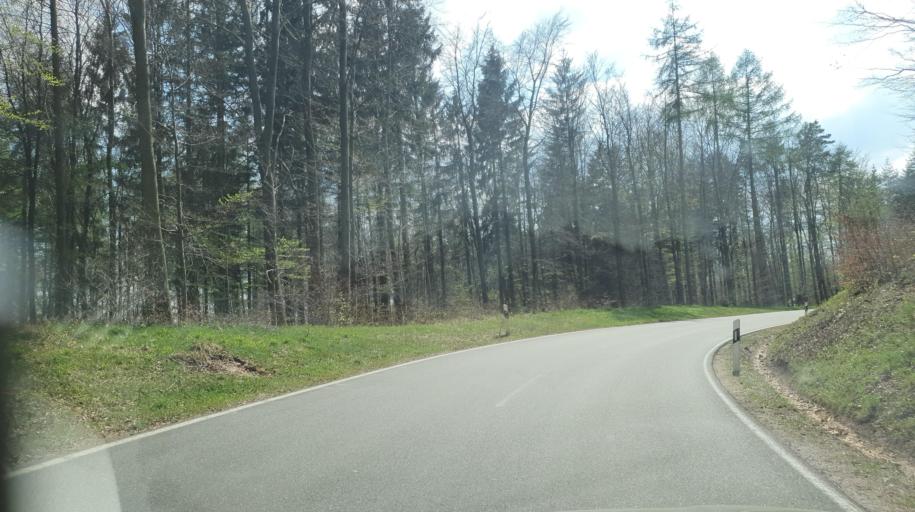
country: DE
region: Rheinland-Pfalz
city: Leimen
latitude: 49.2820
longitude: 7.7900
